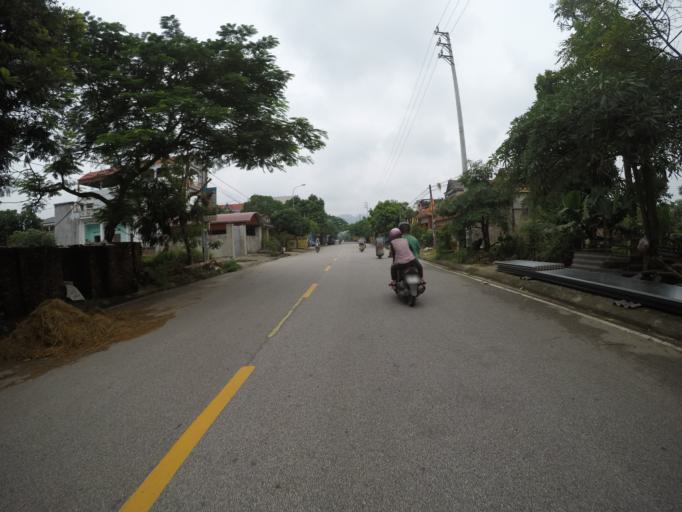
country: VN
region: Ha Noi
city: Soc Son
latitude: 21.2784
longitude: 105.8463
